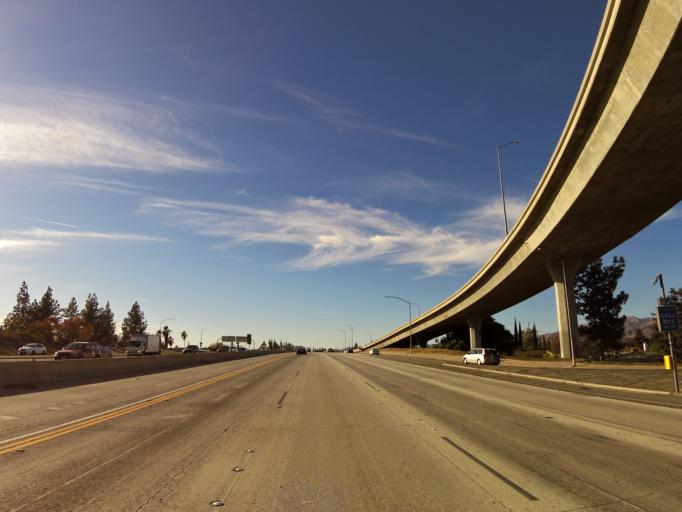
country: US
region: California
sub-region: Los Angeles County
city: San Fernando
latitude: 34.2661
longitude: -118.4734
